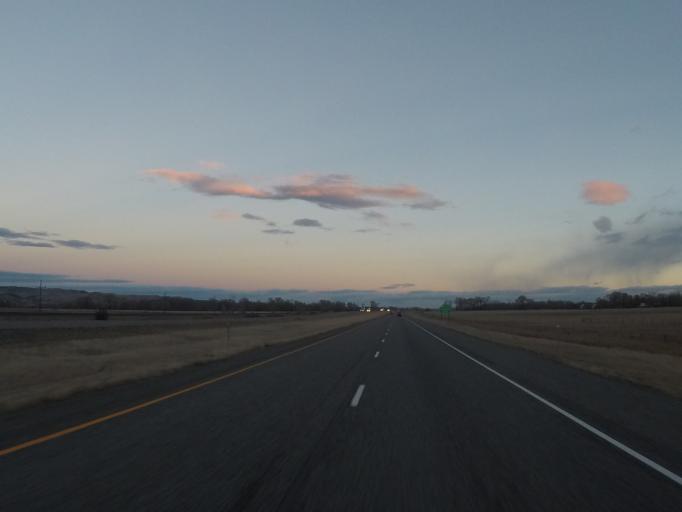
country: US
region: Montana
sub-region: Sweet Grass County
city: Big Timber
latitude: 45.7835
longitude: -109.8129
